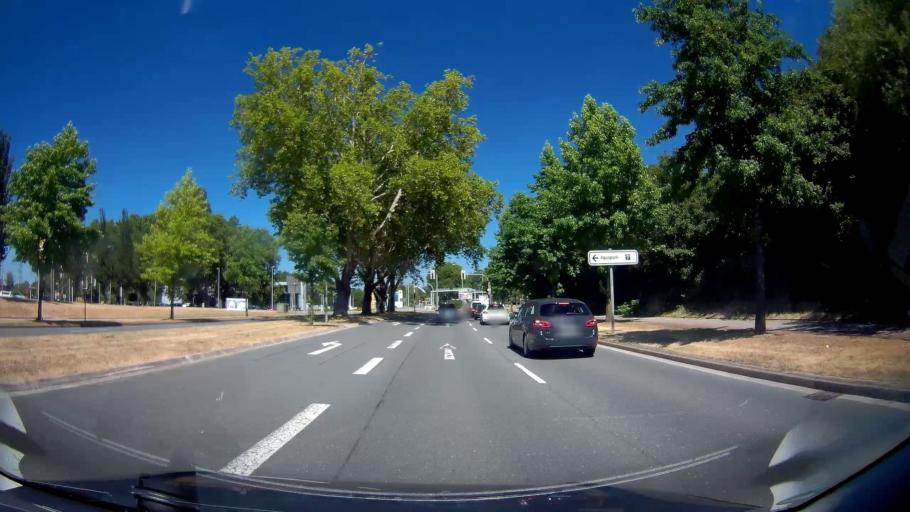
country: DE
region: North Rhine-Westphalia
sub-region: Regierungsbezirk Dusseldorf
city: Oberhausen
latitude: 51.4917
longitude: 6.8870
